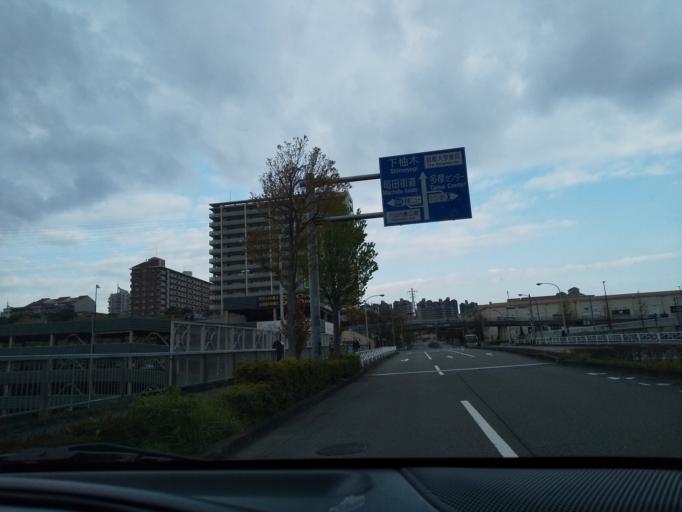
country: JP
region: Tokyo
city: Hino
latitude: 35.6128
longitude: 139.3779
